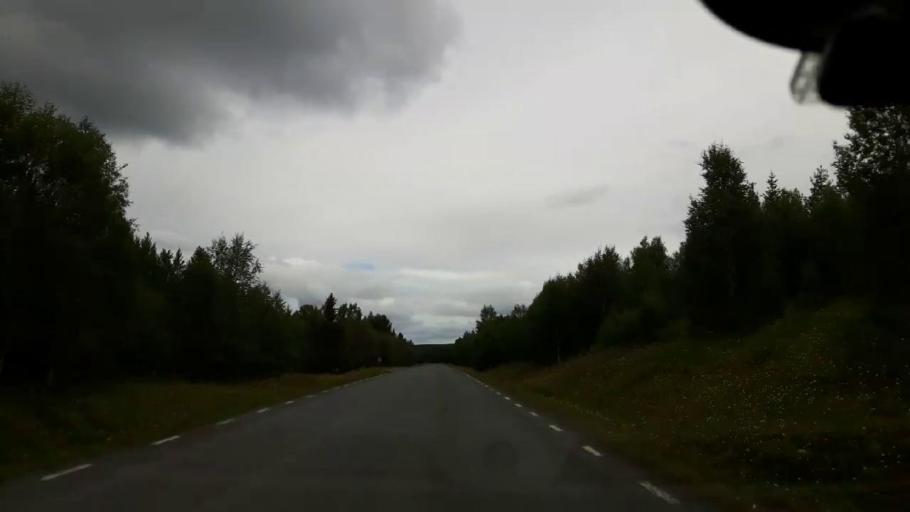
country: SE
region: Jaemtland
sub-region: Krokoms Kommun
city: Valla
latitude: 63.6309
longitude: 13.8168
